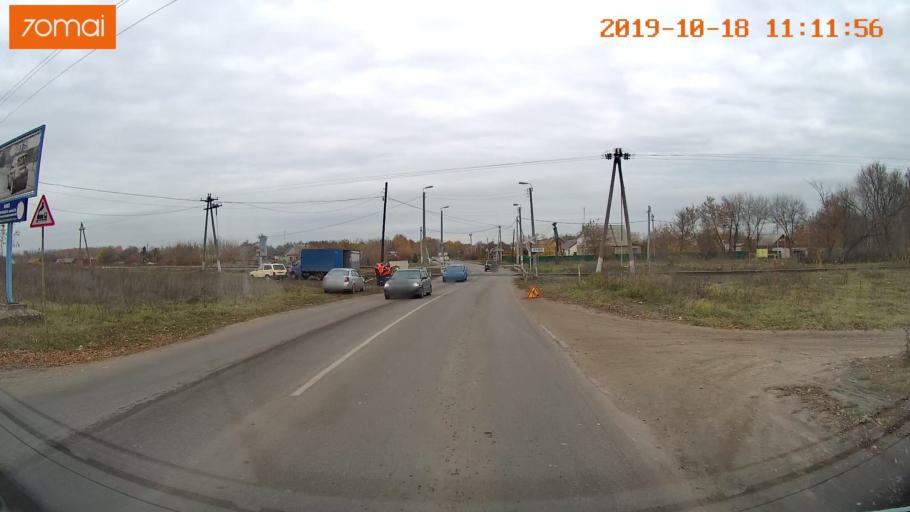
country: RU
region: Tula
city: Kimovsk
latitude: 53.9626
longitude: 38.5517
